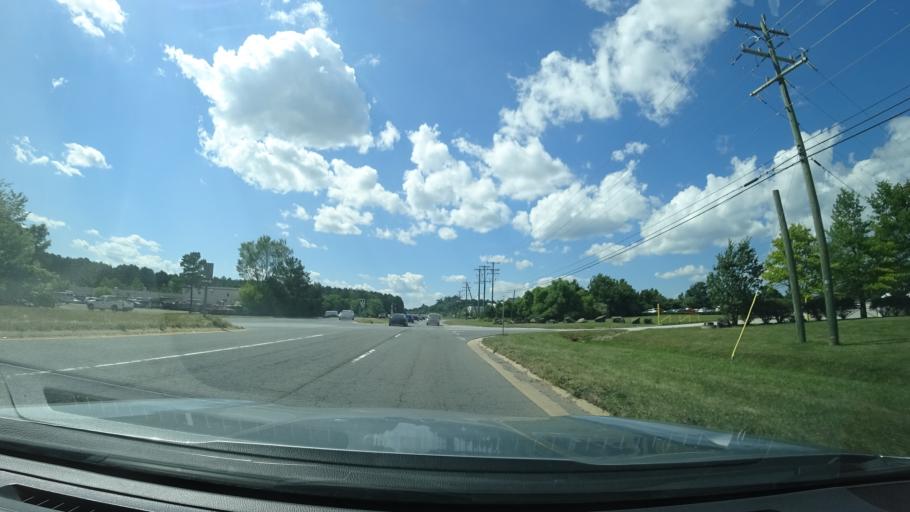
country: US
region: Virginia
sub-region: Loudoun County
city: Sterling
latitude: 38.9842
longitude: -77.4490
